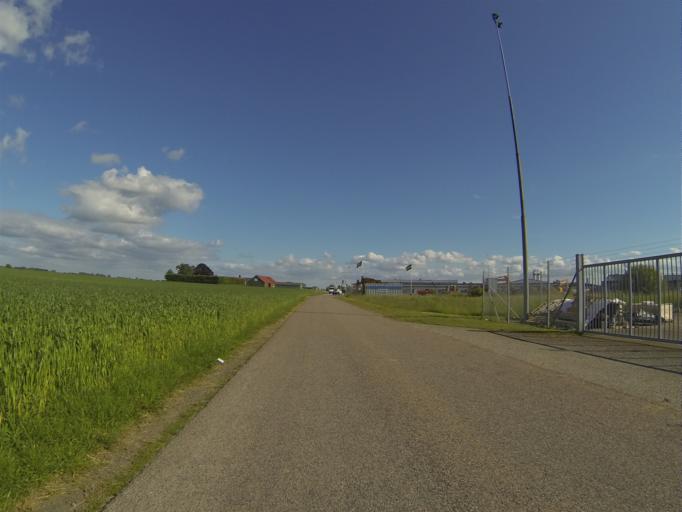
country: SE
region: Skane
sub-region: Staffanstorps Kommun
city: Staffanstorp
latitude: 55.6571
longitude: 13.2329
